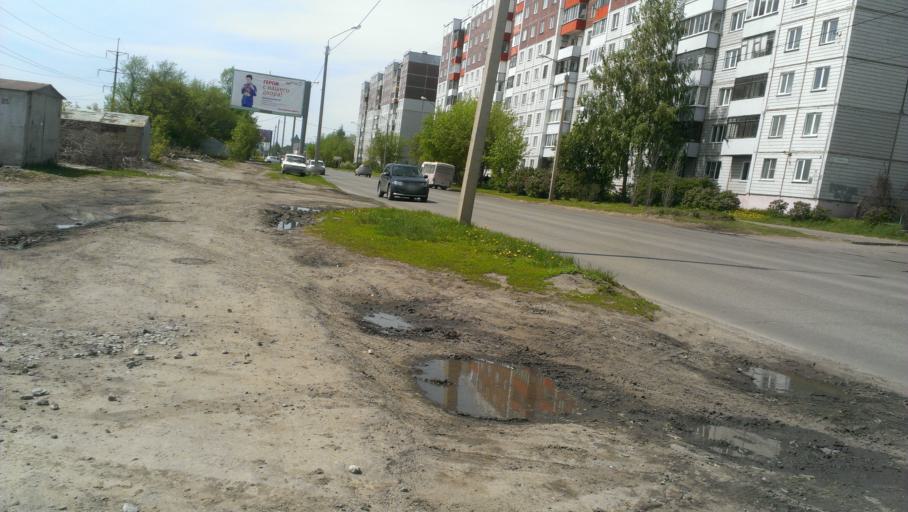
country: RU
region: Altai Krai
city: Novosilikatnyy
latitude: 53.3566
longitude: 83.6636
